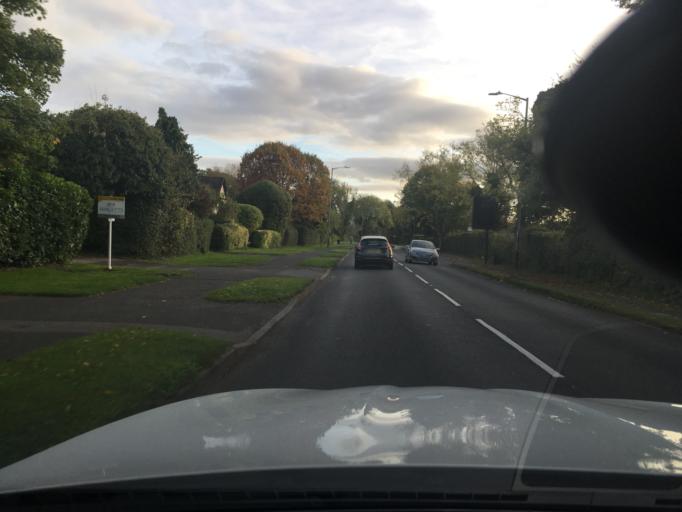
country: GB
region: England
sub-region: Warwickshire
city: Warwick
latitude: 52.2713
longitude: -1.5974
